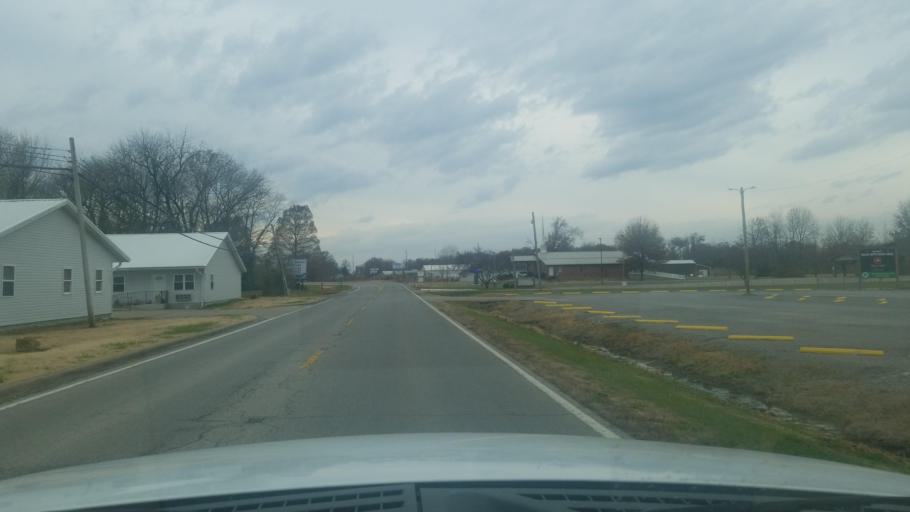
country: US
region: Illinois
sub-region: Saline County
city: Harrisburg
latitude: 37.7389
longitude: -88.5561
